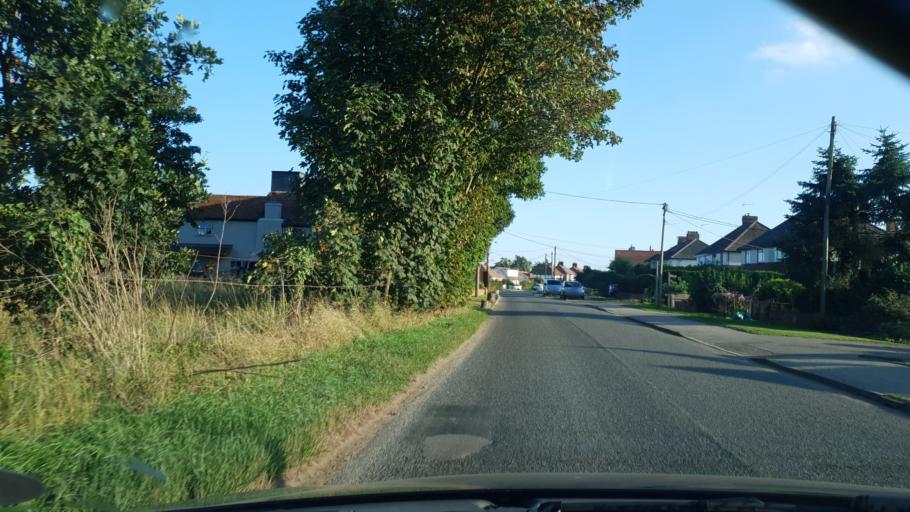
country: GB
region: England
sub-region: Essex
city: Frinton-on-Sea
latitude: 51.8461
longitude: 1.2214
